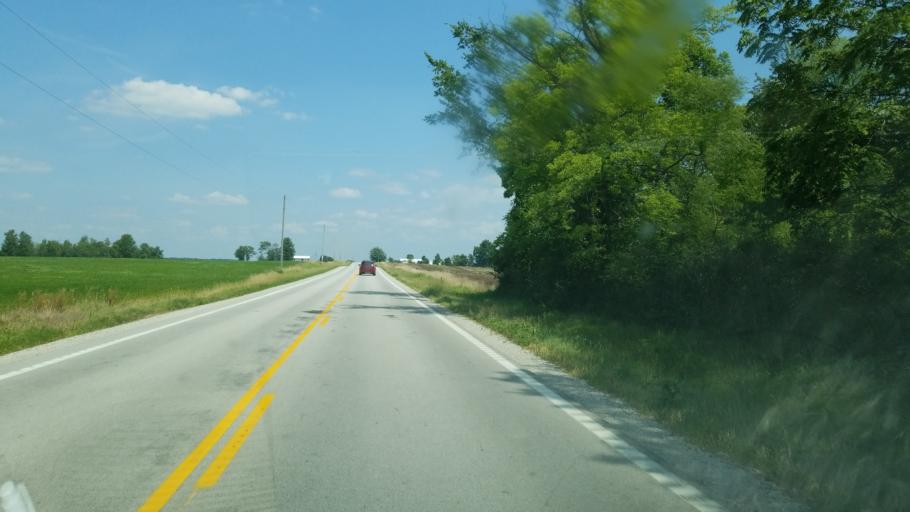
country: US
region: Ohio
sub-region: Sandusky County
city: Mount Carmel
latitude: 41.1248
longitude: -82.9348
